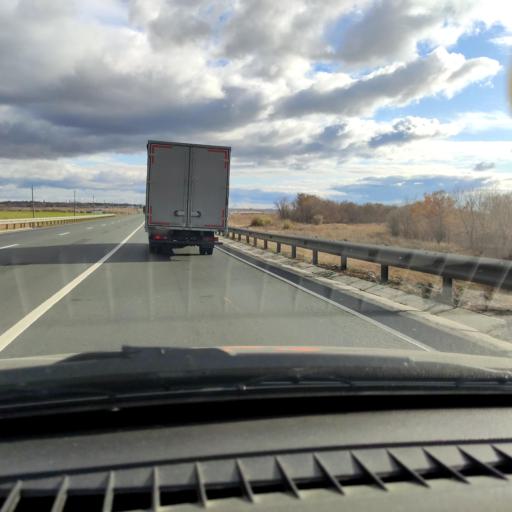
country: RU
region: Samara
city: Varlamovo
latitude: 53.2111
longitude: 48.4699
